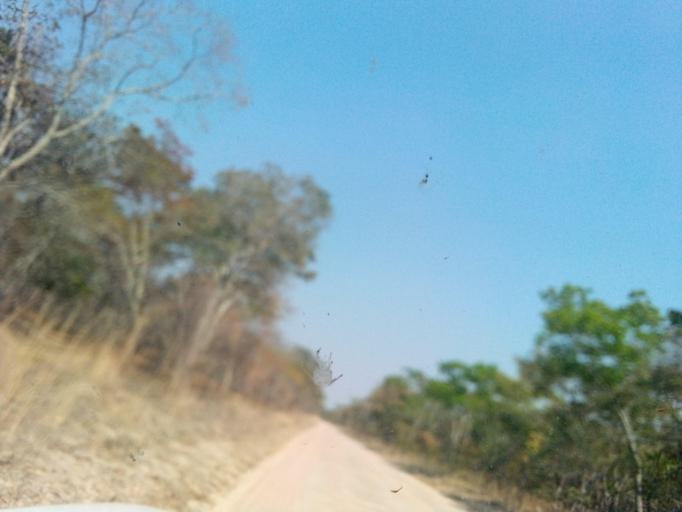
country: ZM
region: Northern
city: Mpika
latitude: -12.2259
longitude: 30.9011
